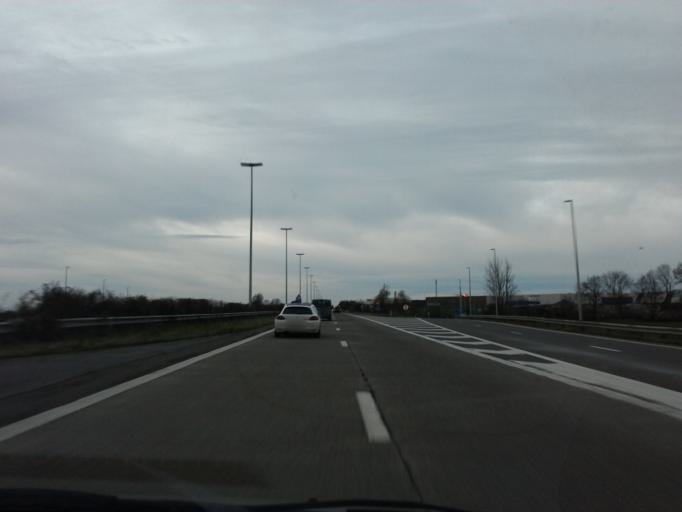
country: BE
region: Wallonia
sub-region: Province de Liege
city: Sprimont
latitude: 50.5080
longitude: 5.6890
